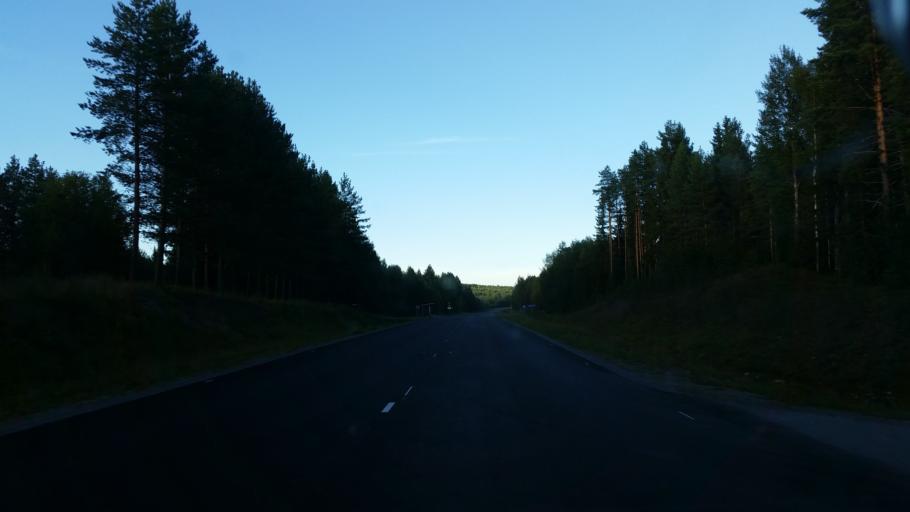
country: SE
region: Vaesterbotten
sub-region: Dorotea Kommun
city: Dorotea
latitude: 64.2940
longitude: 16.5377
